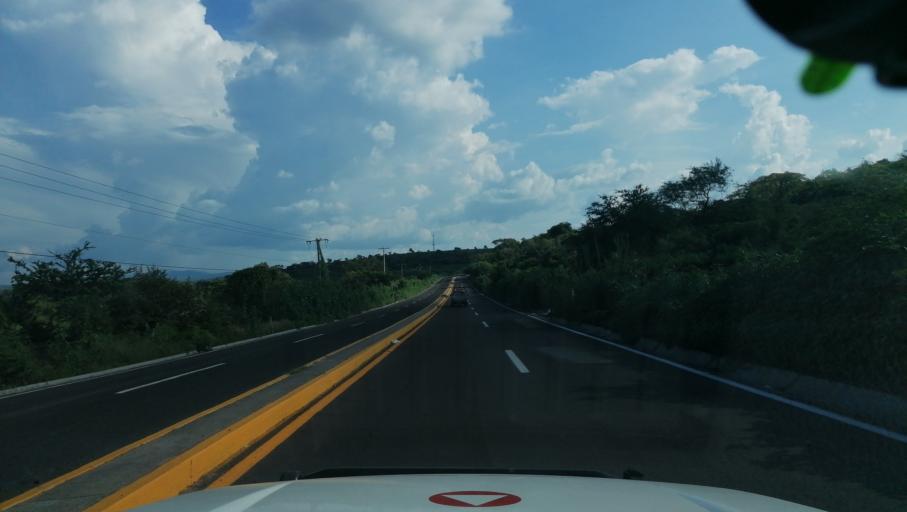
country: MX
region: Morelos
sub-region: Ayala
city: Abelardo L. Rodriguez
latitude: 18.7070
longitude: -98.9910
